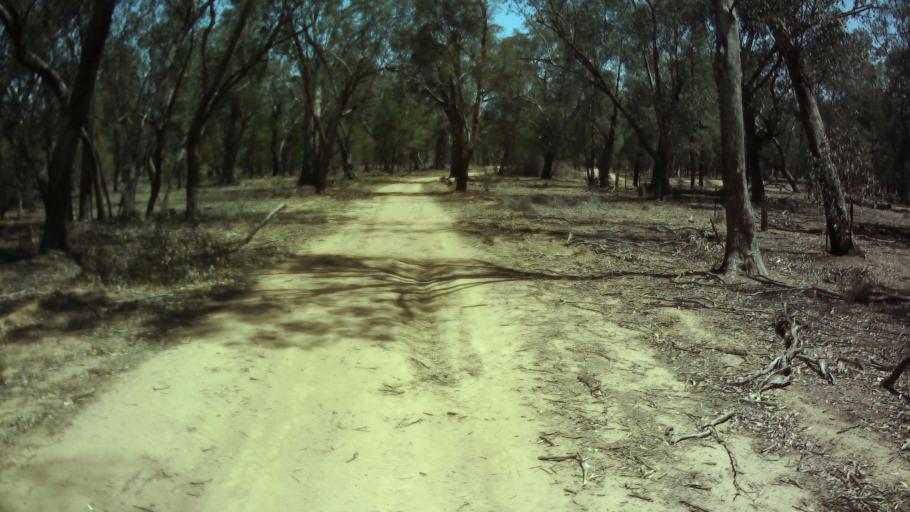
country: AU
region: New South Wales
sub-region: Weddin
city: Grenfell
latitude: -34.0717
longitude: 147.7880
